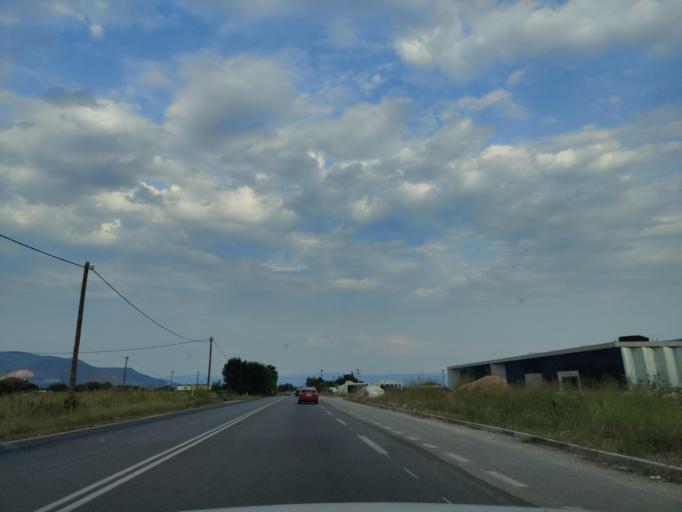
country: GR
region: East Macedonia and Thrace
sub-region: Nomos Dramas
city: Xiropotamos
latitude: 41.1584
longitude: 24.0959
